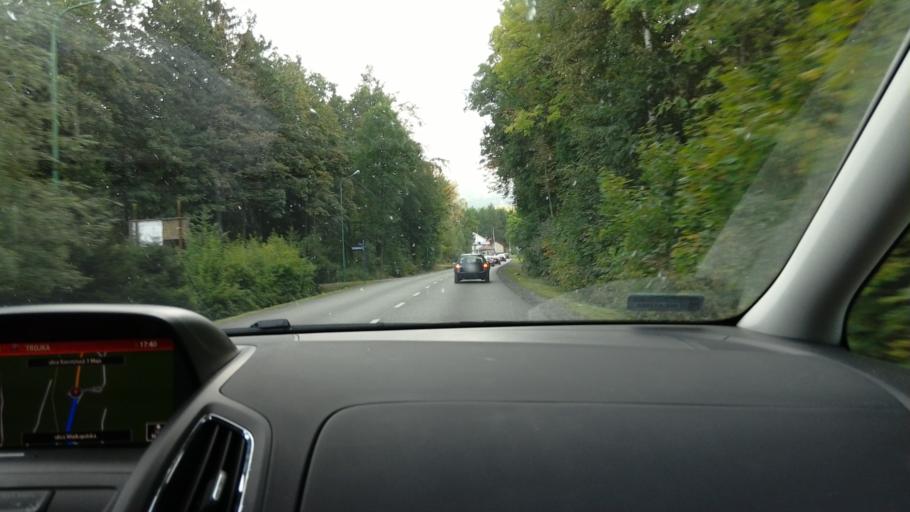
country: PL
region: Lower Silesian Voivodeship
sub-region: Powiat jeleniogorski
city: Karpacz
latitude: 50.7890
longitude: 15.7601
